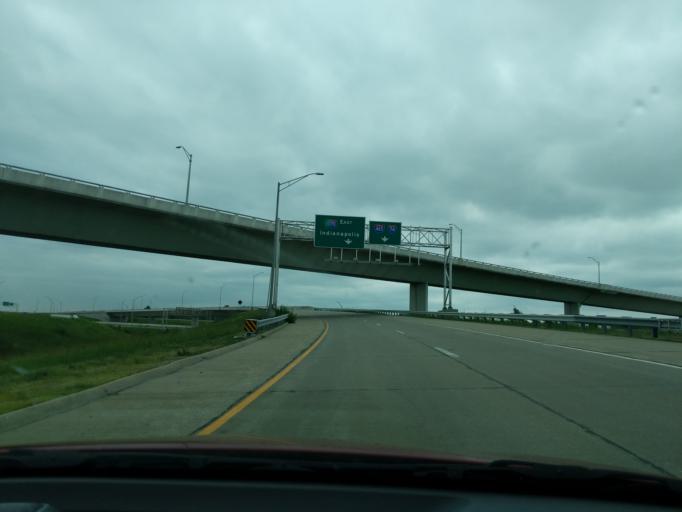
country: US
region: Indiana
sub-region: Hendricks County
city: Plainfield
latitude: 39.6926
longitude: -86.3183
